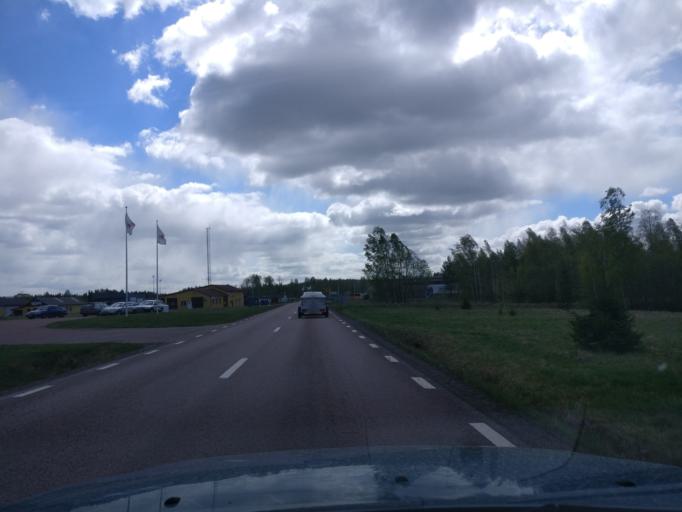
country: SE
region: Vaermland
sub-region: Karlstads Kommun
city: Molkom
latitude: 59.6086
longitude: 13.7370
